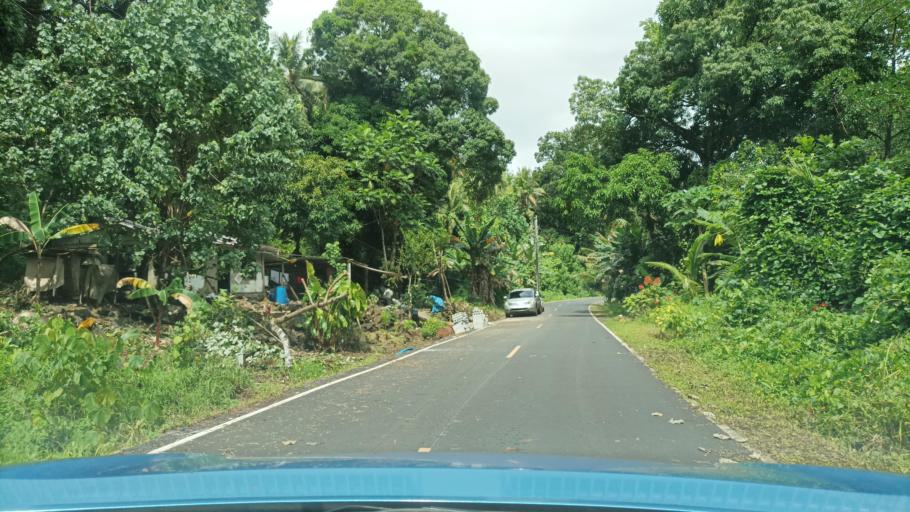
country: FM
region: Pohnpei
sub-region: Madolenihm Municipality
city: Madolenihm Municipality Government
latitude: 6.8780
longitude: 158.3321
